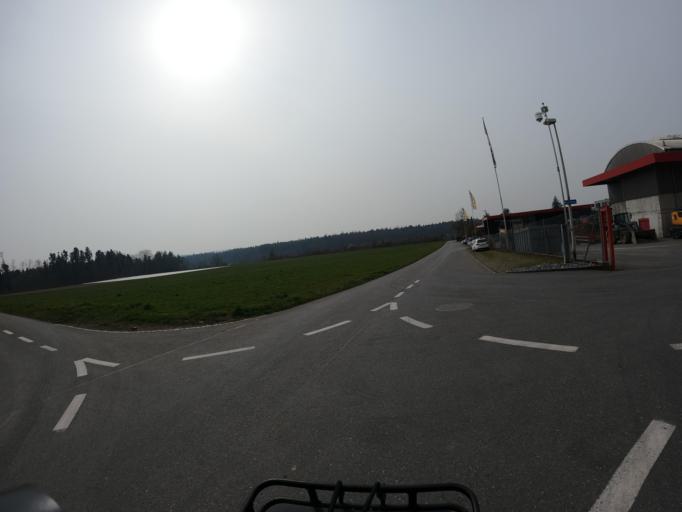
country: CH
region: Aargau
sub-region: Bezirk Lenzburg
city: Niederlenz
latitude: 47.4134
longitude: 8.1928
